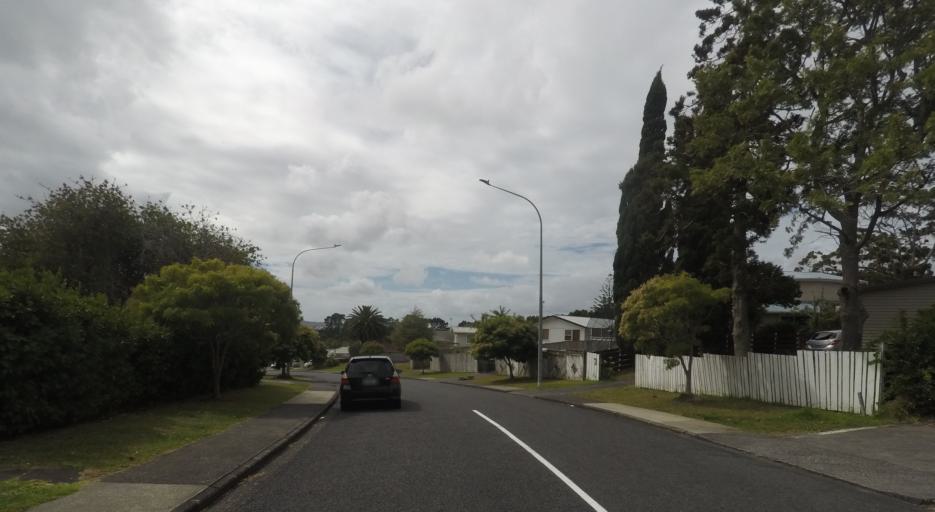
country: NZ
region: Auckland
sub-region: Auckland
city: Rosebank
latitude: -36.8892
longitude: 174.6494
